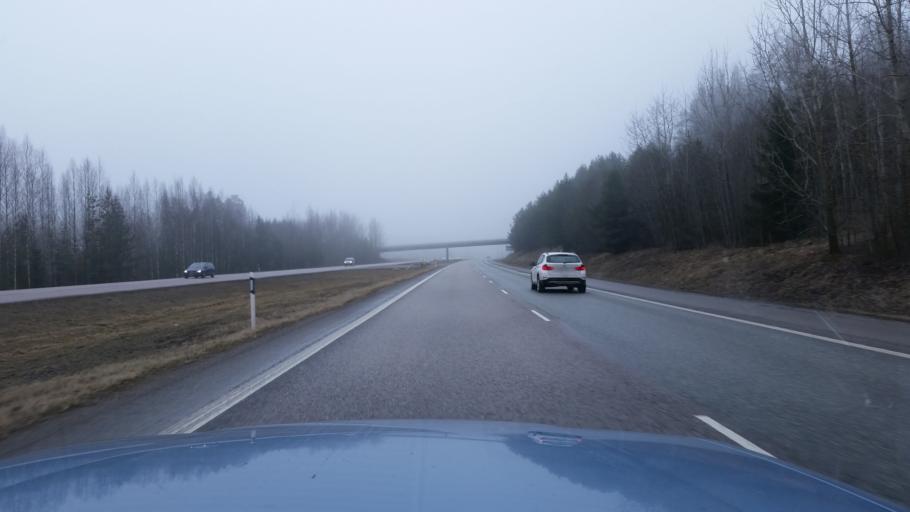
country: FI
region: Uusimaa
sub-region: Helsinki
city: Nurmijaervi
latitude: 60.4653
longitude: 24.8493
